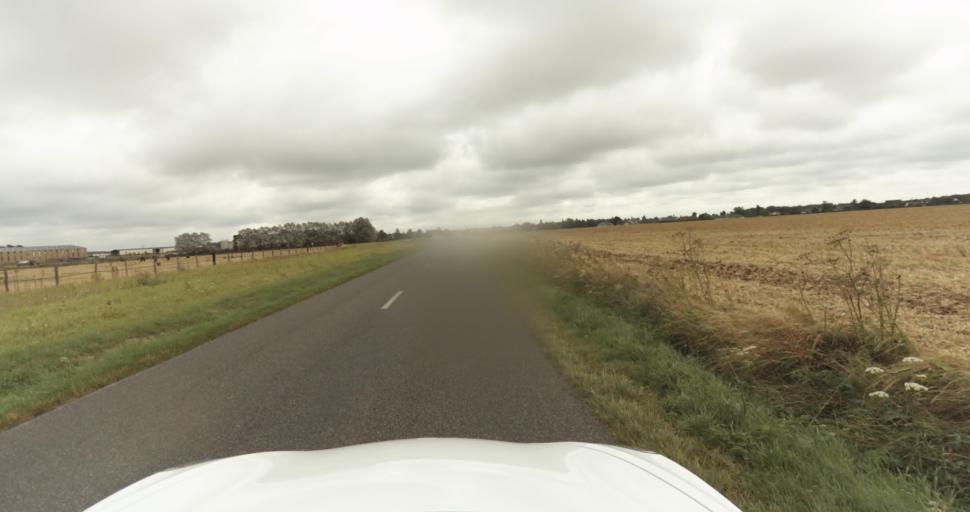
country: FR
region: Haute-Normandie
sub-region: Departement de l'Eure
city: Aviron
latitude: 49.0596
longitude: 1.0802
